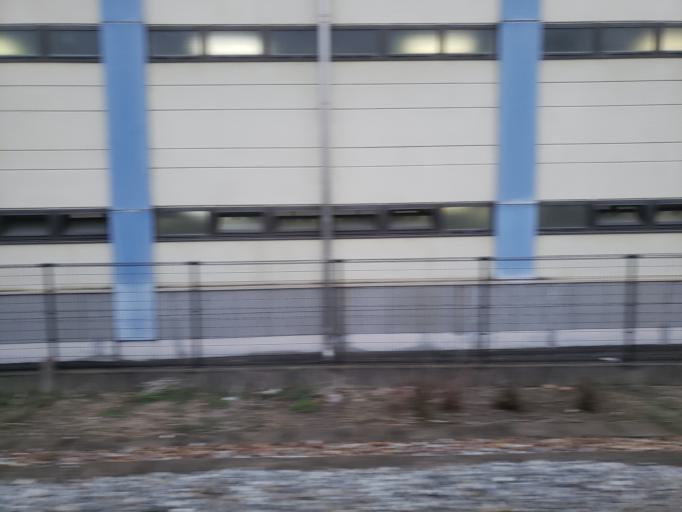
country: JP
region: Hyogo
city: Akashi
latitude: 34.6814
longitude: 134.9397
